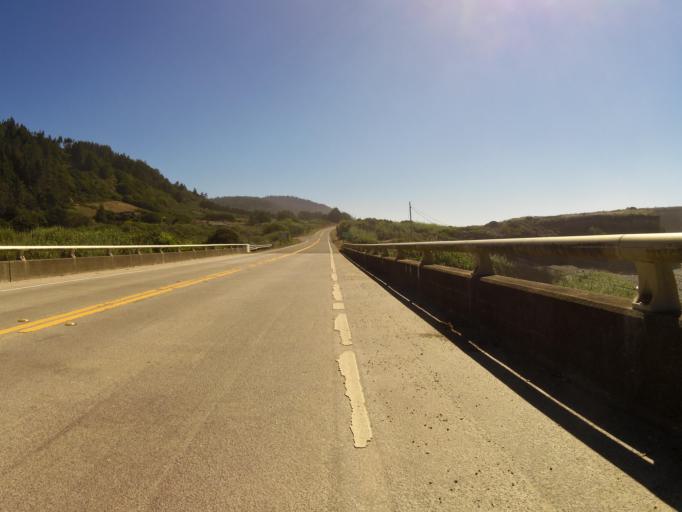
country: US
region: California
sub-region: Mendocino County
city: Fort Bragg
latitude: 39.6594
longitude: -123.7852
